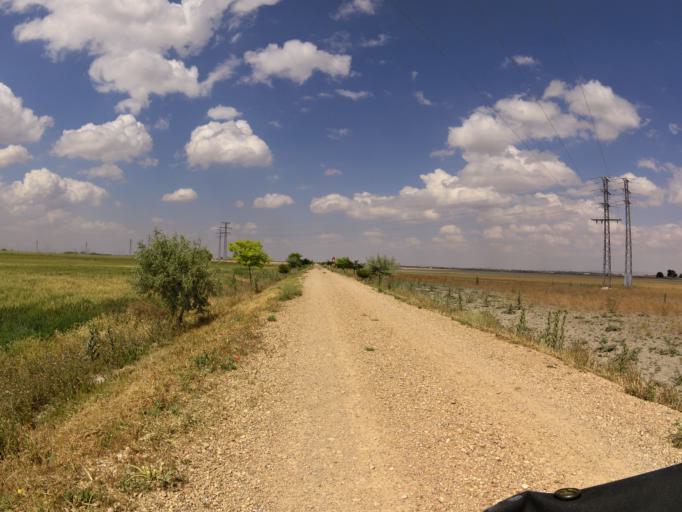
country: ES
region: Castille-La Mancha
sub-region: Provincia de Albacete
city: Albacete
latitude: 38.9324
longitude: -1.9917
